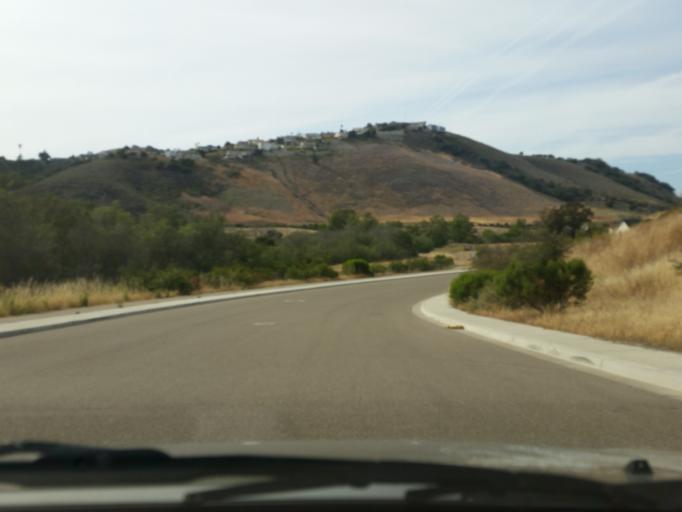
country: US
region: California
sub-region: San Luis Obispo County
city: Pismo Beach
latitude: 35.1453
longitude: -120.6301
